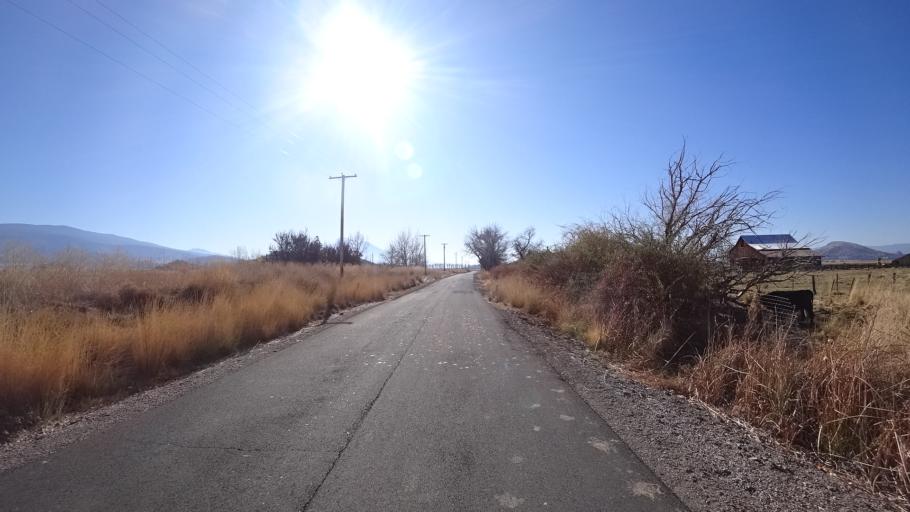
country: US
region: California
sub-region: Siskiyou County
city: Montague
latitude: 41.7004
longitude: -122.3762
